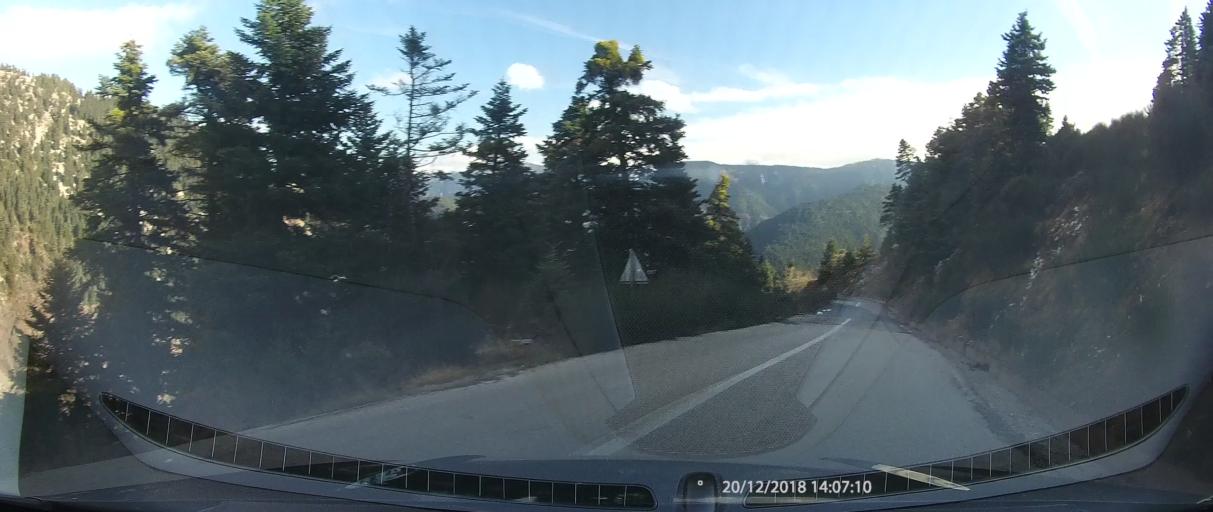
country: GR
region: West Greece
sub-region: Nomos Aitolias kai Akarnanias
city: Thermo
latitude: 38.7538
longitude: 21.6462
